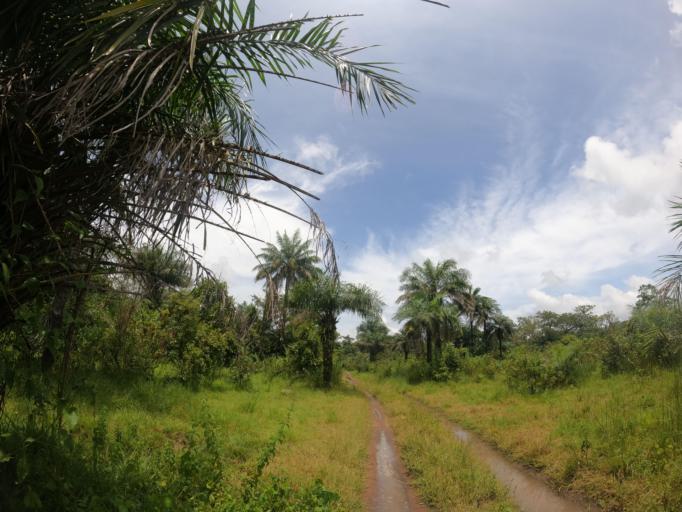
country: SL
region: Northern Province
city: Binkolo
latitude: 9.1385
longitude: -12.2382
